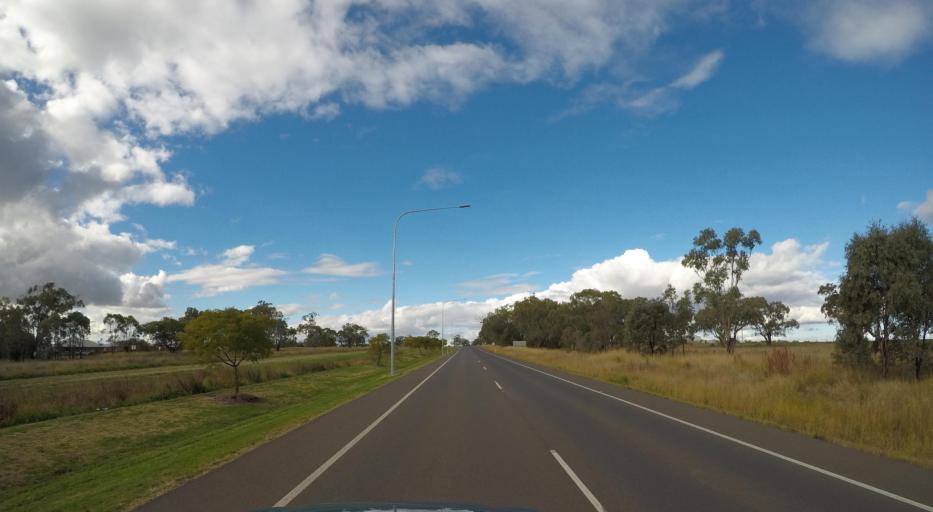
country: AU
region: Queensland
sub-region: Toowoomba
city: Westbrook
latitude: -27.7197
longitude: 151.6162
